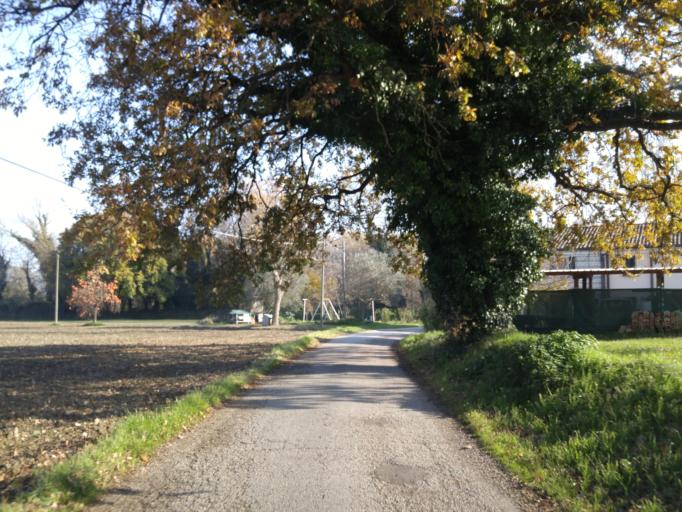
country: IT
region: The Marches
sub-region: Provincia di Pesaro e Urbino
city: Calcinelli
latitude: 43.7481
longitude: 12.9256
